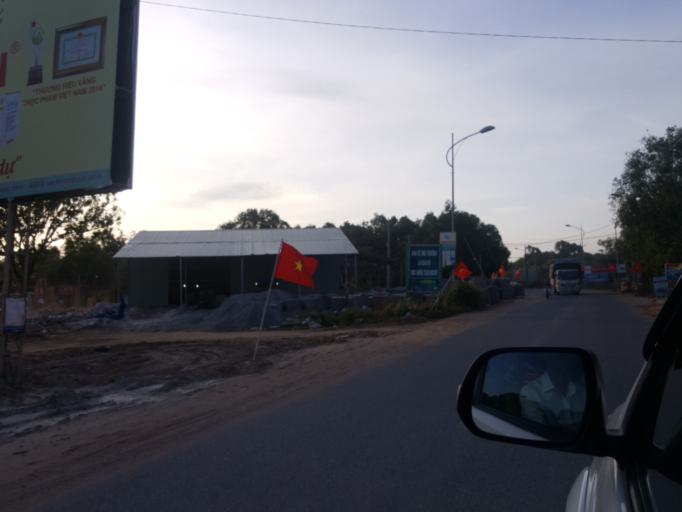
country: VN
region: Kien Giang
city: Duong GJong
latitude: 10.1528
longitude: 104.0329
